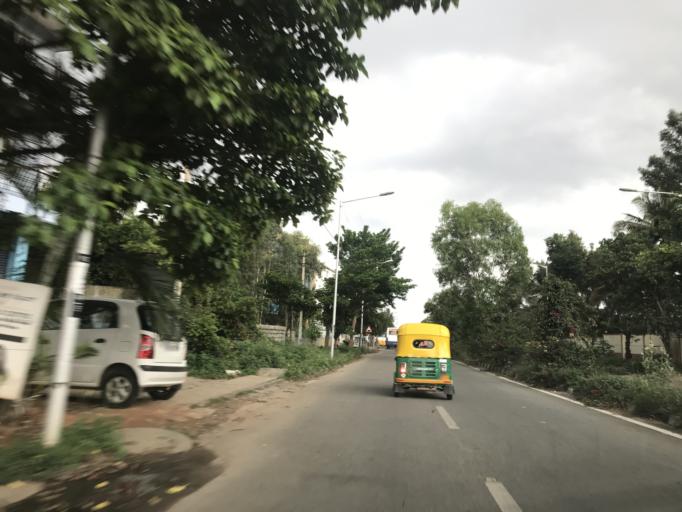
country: IN
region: Karnataka
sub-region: Bangalore Urban
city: Yelahanka
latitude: 13.1233
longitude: 77.6381
